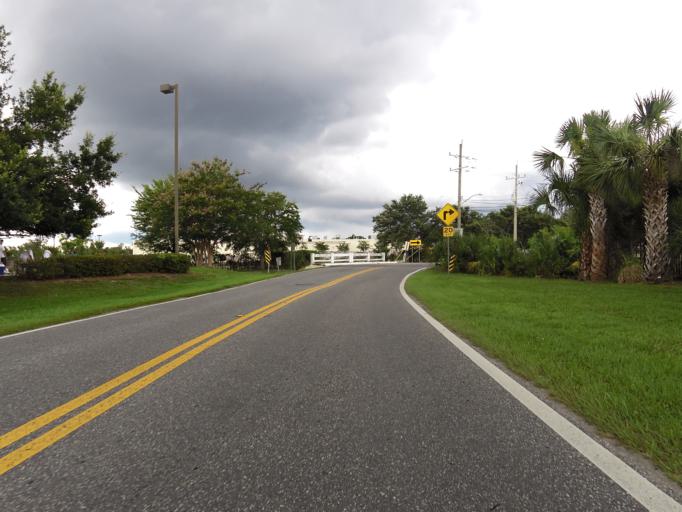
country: US
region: Florida
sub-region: Duval County
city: Jacksonville
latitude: 30.2782
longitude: -81.7177
